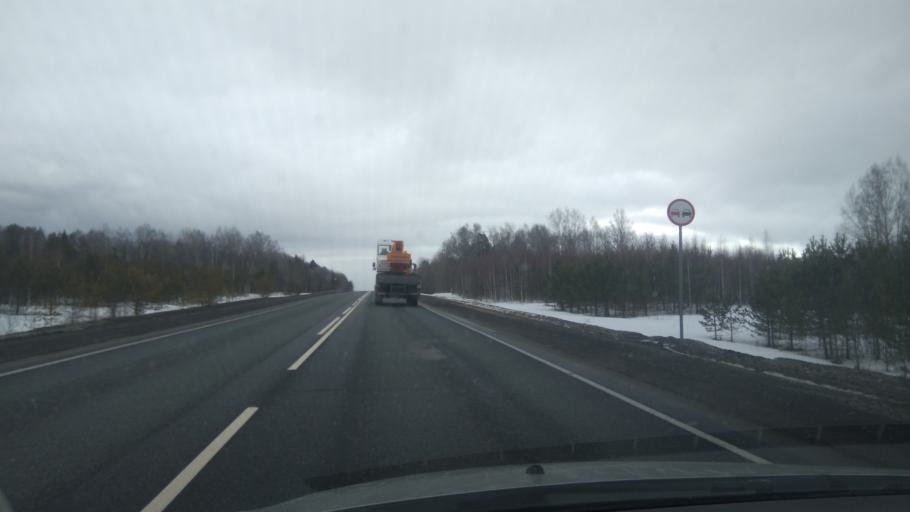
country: RU
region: Perm
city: Suksun
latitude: 56.9915
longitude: 57.4899
